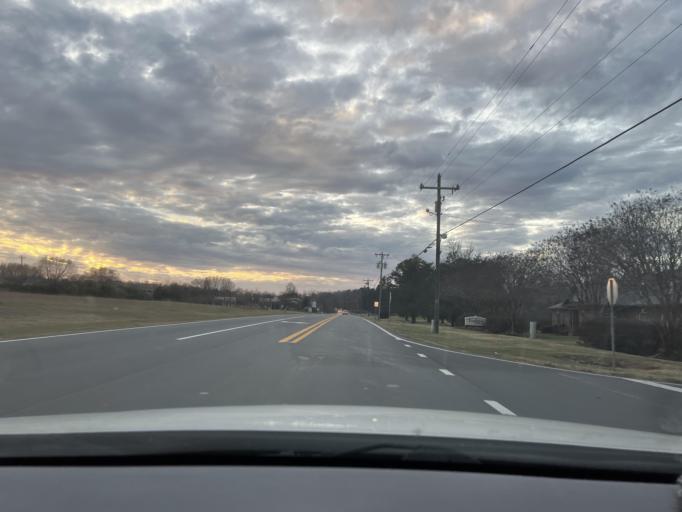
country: US
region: North Carolina
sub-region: Guilford County
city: Gibsonville
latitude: 36.0791
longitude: -79.5531
